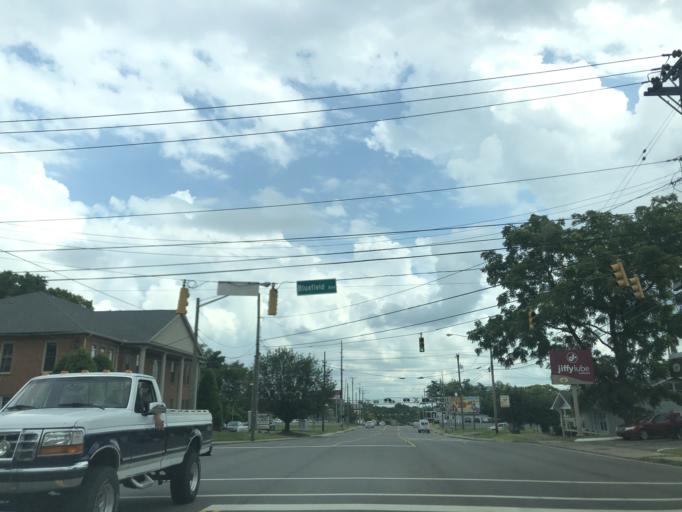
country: US
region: Tennessee
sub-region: Davidson County
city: Lakewood
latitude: 36.1644
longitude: -86.6639
